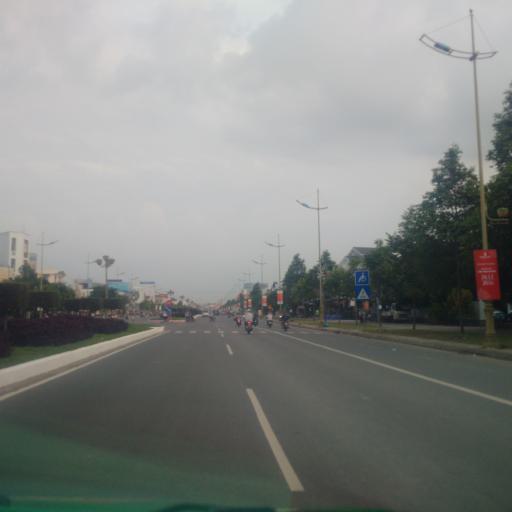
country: VN
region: Can Tho
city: Binh Thuy
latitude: 10.0669
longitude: 105.7308
